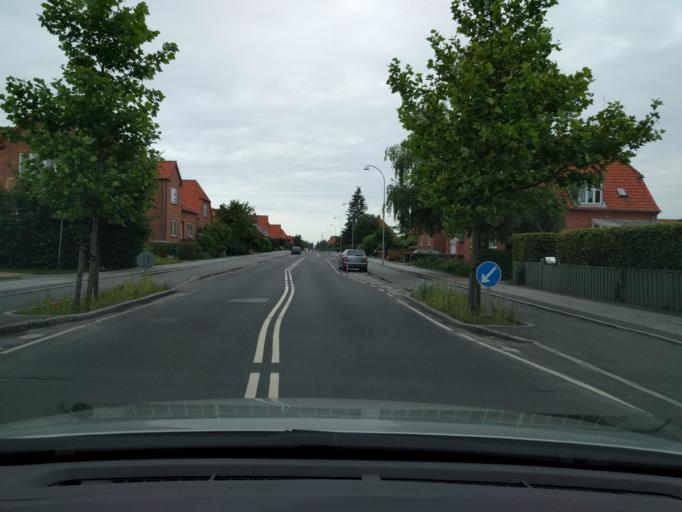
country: DK
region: Zealand
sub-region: Roskilde Kommune
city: Roskilde
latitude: 55.6400
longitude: 12.0684
